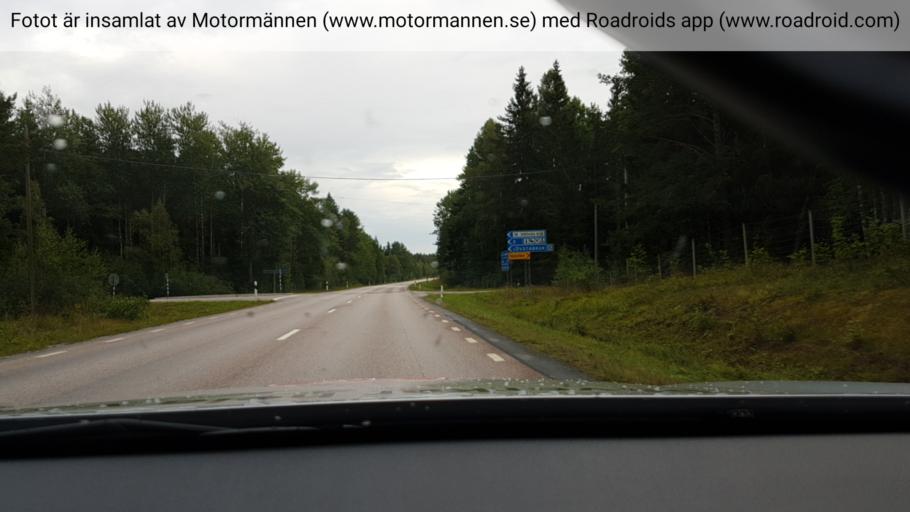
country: SE
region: Uppsala
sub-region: Osthammars Kommun
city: Osterbybruk
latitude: 60.4223
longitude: 17.8504
